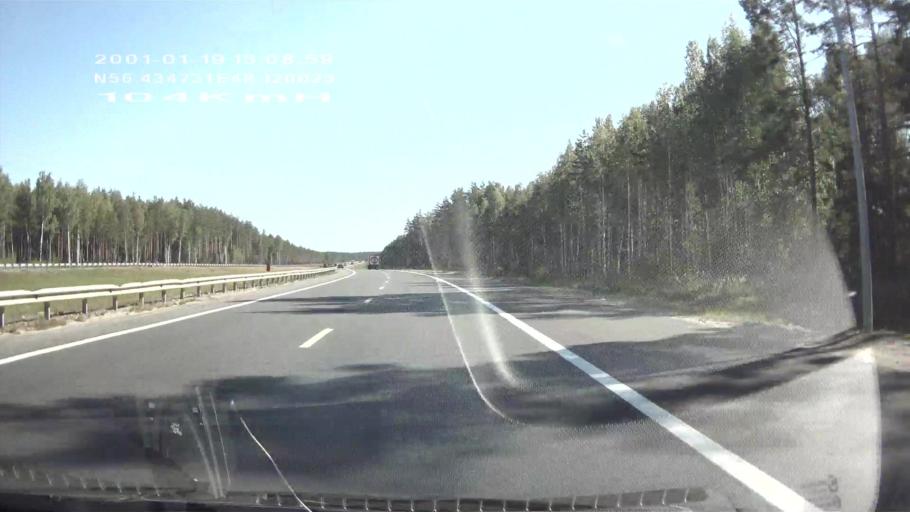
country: RU
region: Mariy-El
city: Surok
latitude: 56.4344
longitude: 48.1204
